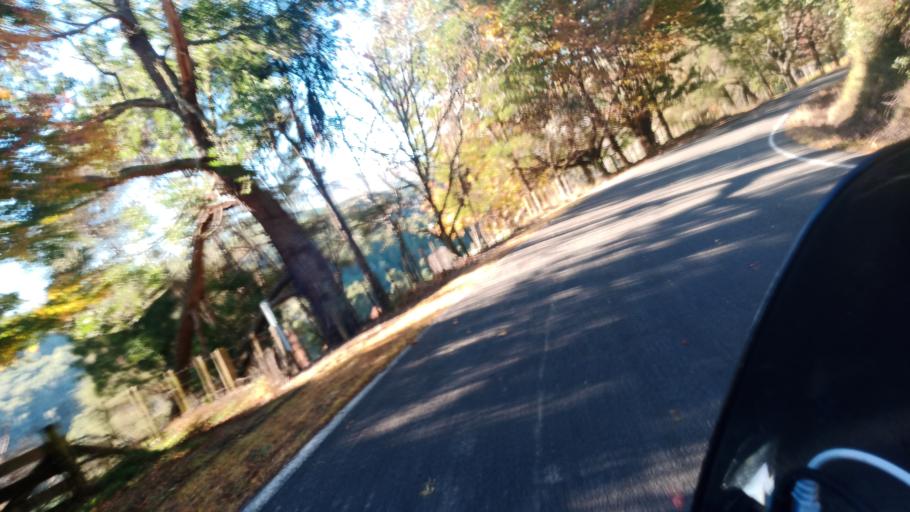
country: NZ
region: Hawke's Bay
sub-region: Wairoa District
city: Wairoa
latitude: -38.8186
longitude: 177.2936
